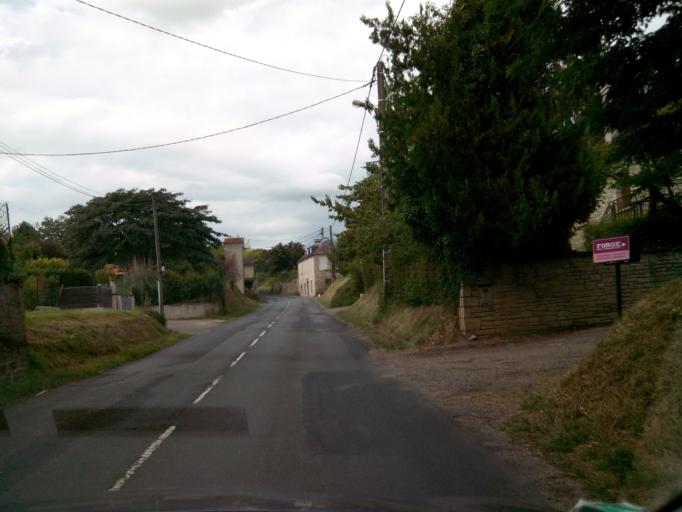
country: FR
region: Midi-Pyrenees
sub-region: Departement du Lot
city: Vayrac
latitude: 44.9573
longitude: 1.7034
